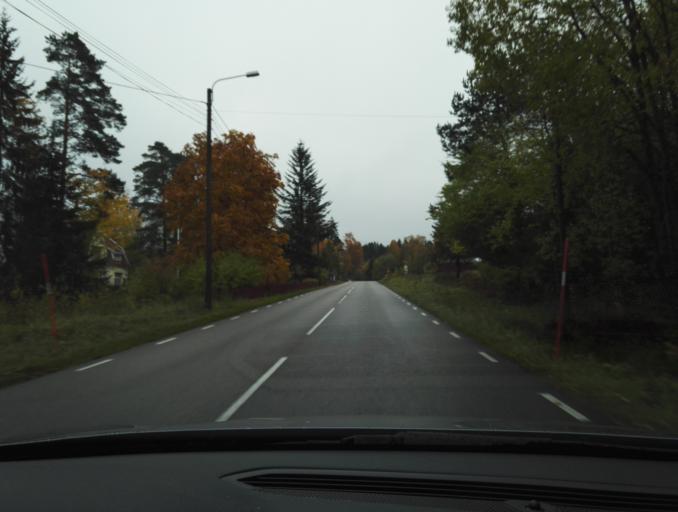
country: SE
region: Kronoberg
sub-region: Vaxjo Kommun
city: Rottne
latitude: 57.0297
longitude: 14.8172
